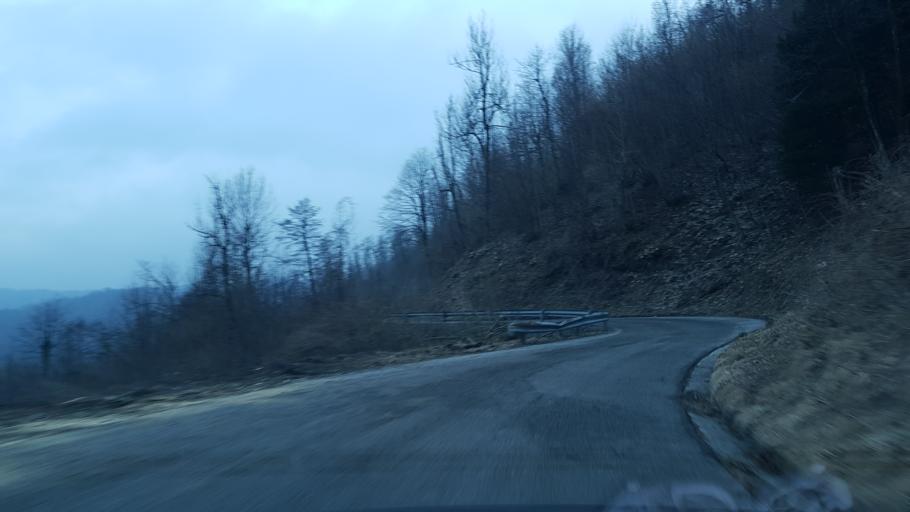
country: IT
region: Friuli Venezia Giulia
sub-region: Provincia di Udine
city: Taipana
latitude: 46.2122
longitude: 13.3561
